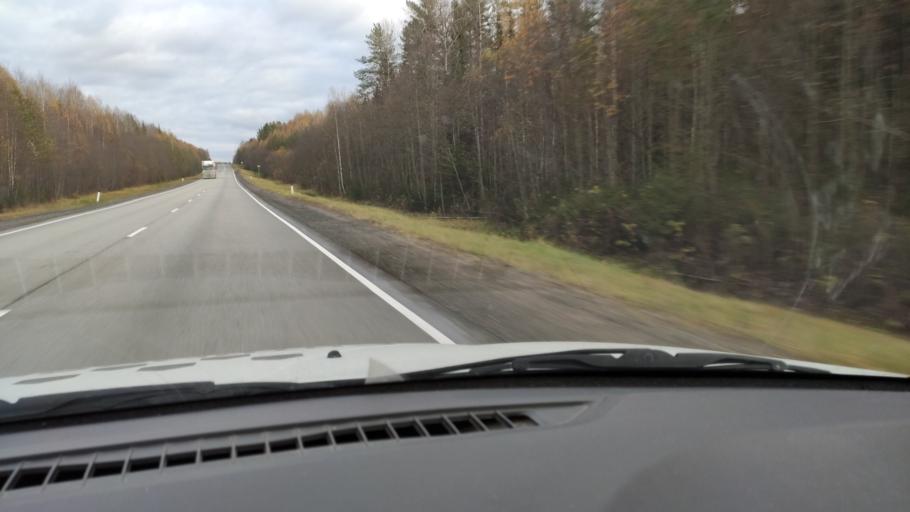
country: RU
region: Kirov
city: Dubrovka
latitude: 58.9008
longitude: 51.2972
